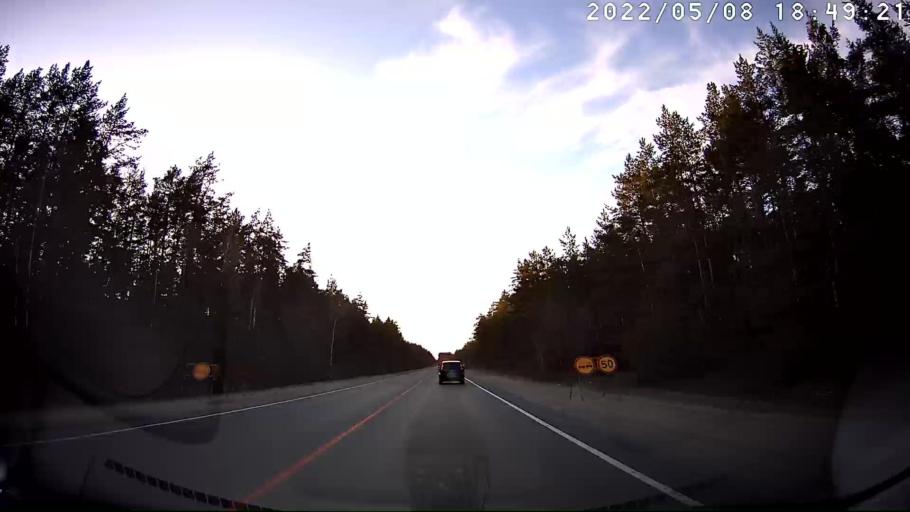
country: RU
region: Mariy-El
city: Krasnogorskiy
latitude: 56.0682
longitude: 48.3650
